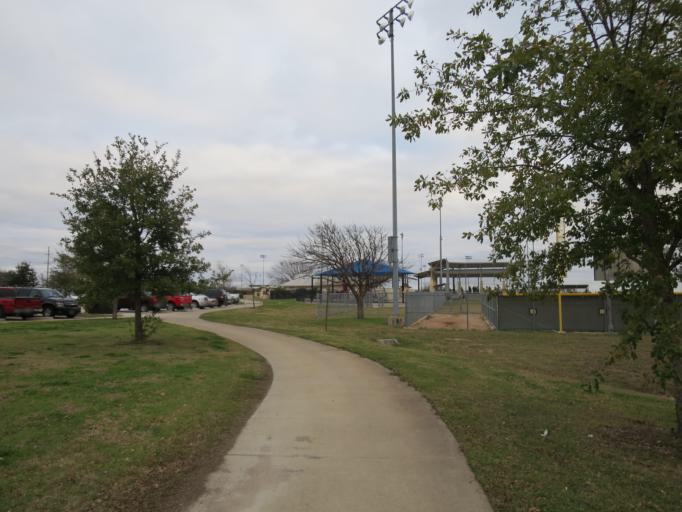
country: US
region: Texas
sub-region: Williamson County
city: Round Rock
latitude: 30.5443
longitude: -97.6199
